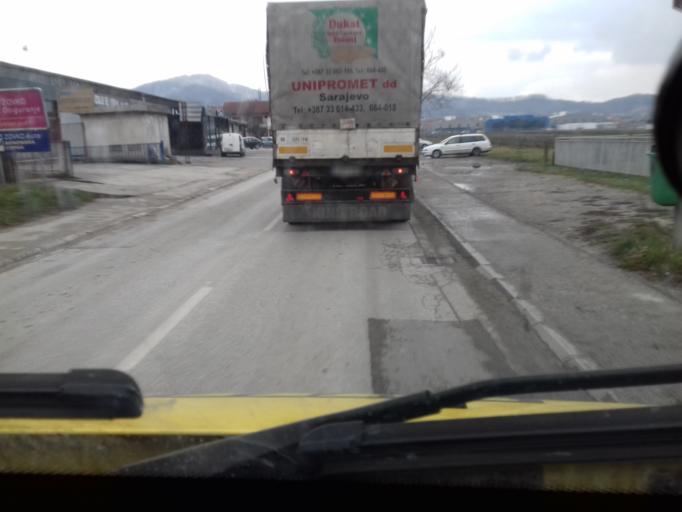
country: BA
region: Federation of Bosnia and Herzegovina
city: Zepce
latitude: 44.4247
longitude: 18.0407
